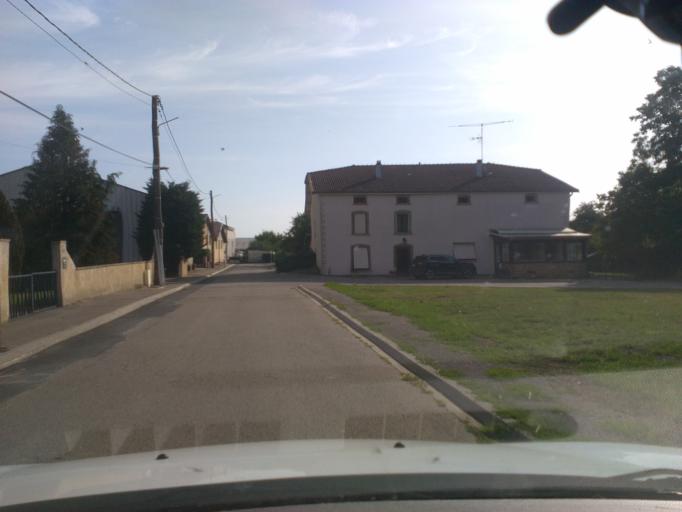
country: FR
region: Lorraine
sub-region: Departement des Vosges
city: Mirecourt
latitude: 48.3325
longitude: 6.0968
